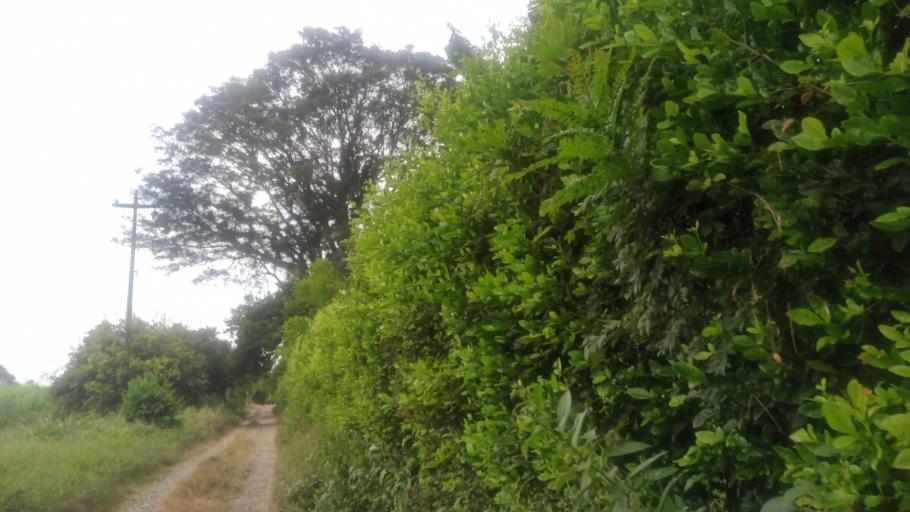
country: CO
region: Cauca
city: Puerto Tejada
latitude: 3.2669
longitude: -76.4687
